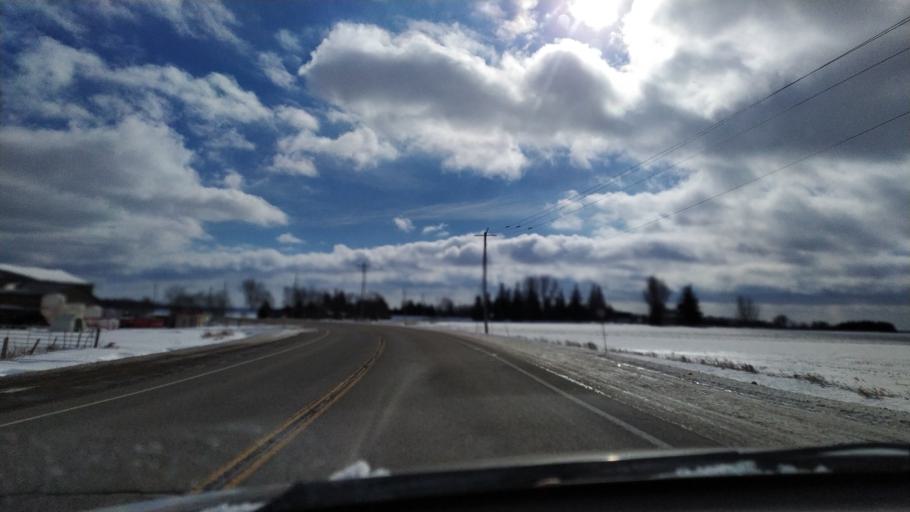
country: CA
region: Ontario
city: Waterloo
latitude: 43.5833
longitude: -80.6097
